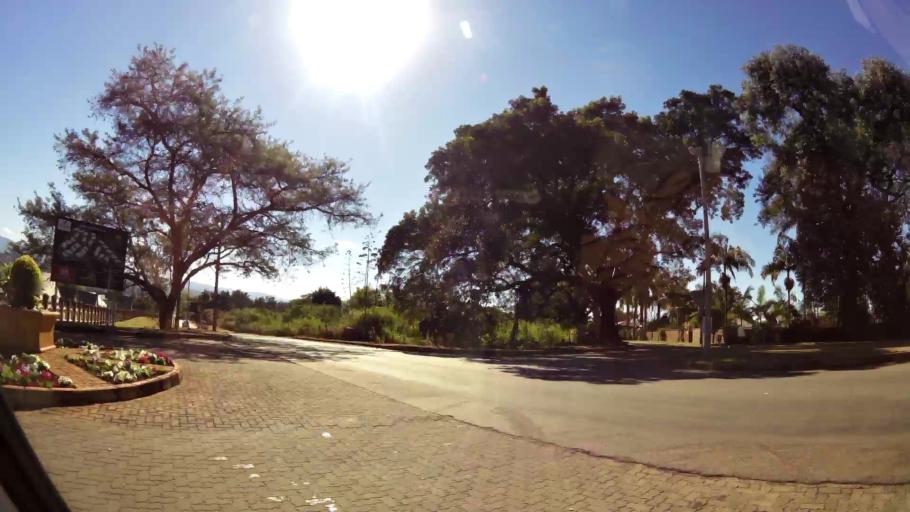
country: ZA
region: Limpopo
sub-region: Mopani District Municipality
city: Tzaneen
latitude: -23.8254
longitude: 30.1428
